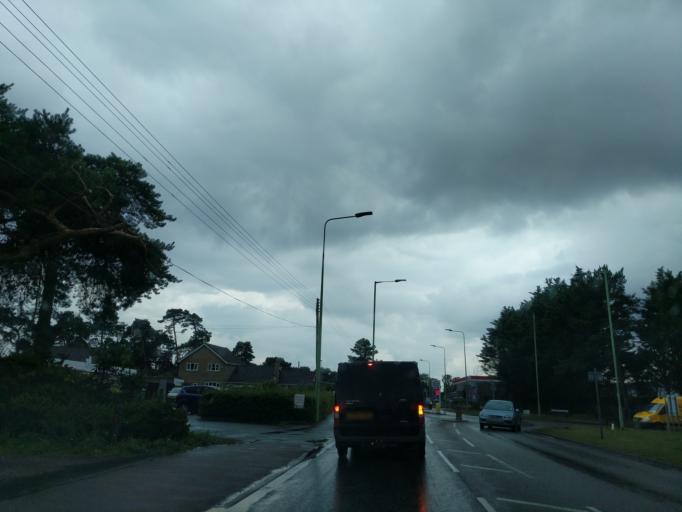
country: GB
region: England
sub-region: Suffolk
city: Lakenheath
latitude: 52.3556
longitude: 0.5143
